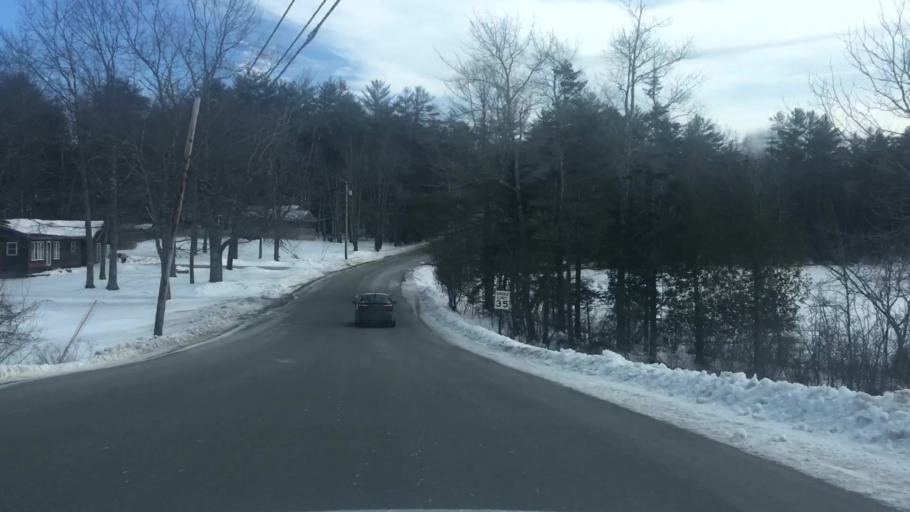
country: US
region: Maine
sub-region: Hancock County
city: Orland
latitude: 44.6301
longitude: -68.7028
